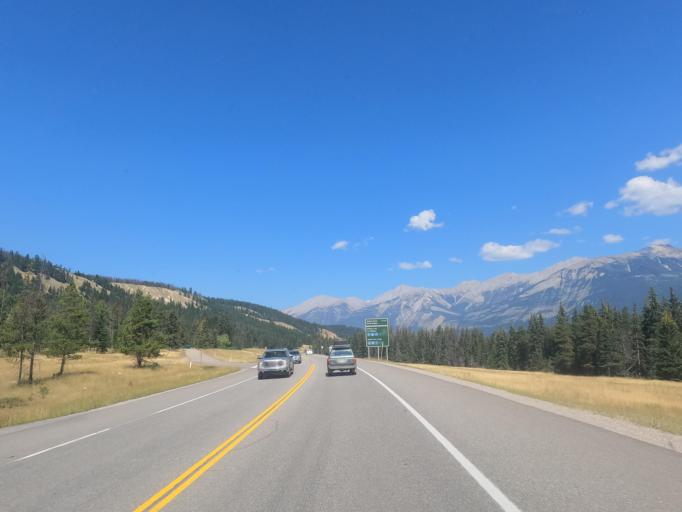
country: CA
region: Alberta
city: Jasper Park Lodge
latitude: 52.8984
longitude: -118.0667
